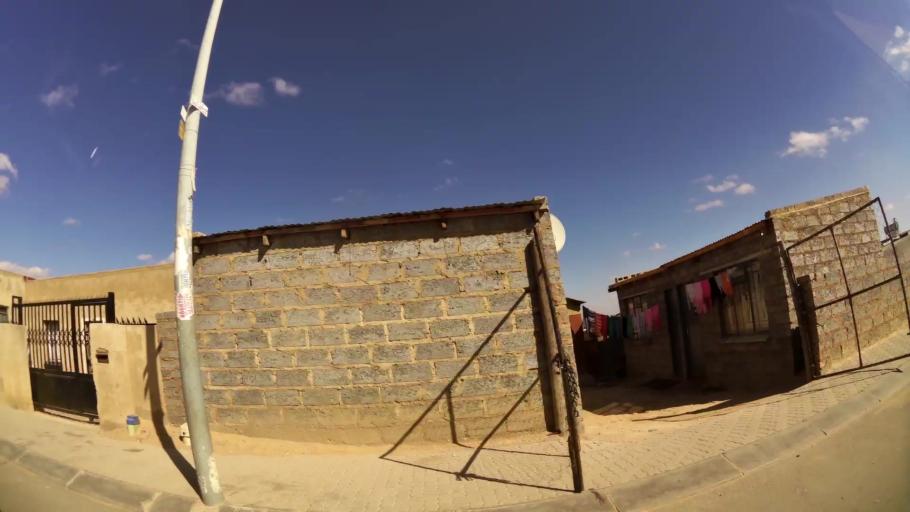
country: ZA
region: Gauteng
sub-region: City of Johannesburg Metropolitan Municipality
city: Modderfontein
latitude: -26.0327
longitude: 28.1730
